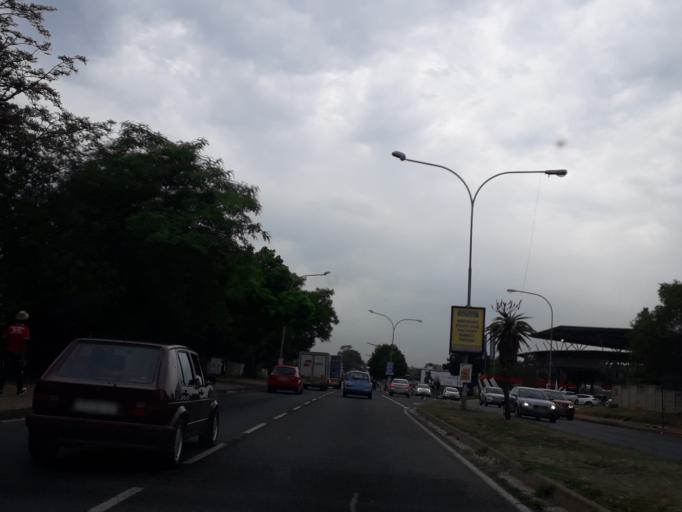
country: ZA
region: Gauteng
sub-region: City of Johannesburg Metropolitan Municipality
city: Roodepoort
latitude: -26.1242
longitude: 27.9640
